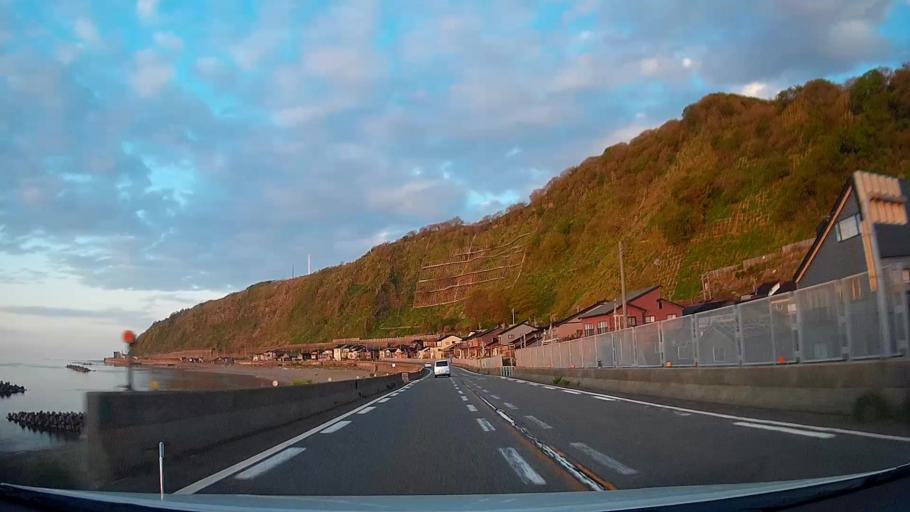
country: JP
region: Niigata
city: Joetsu
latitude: 37.1353
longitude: 138.0542
